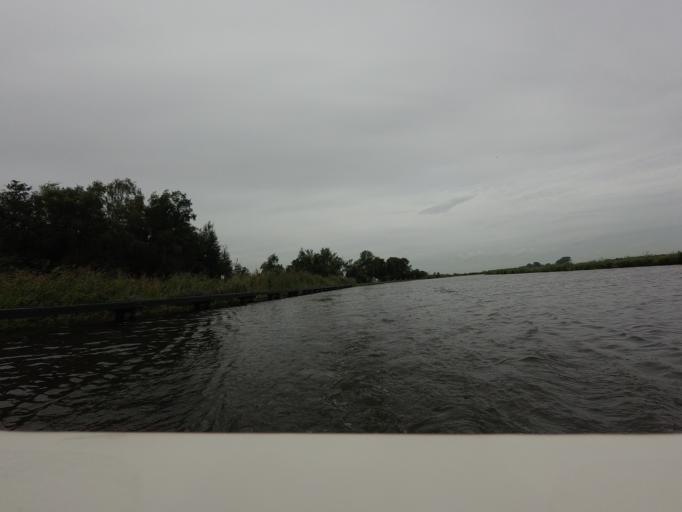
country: NL
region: Friesland
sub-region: Gemeente Boarnsterhim
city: Warten
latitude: 53.1149
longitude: 5.8871
